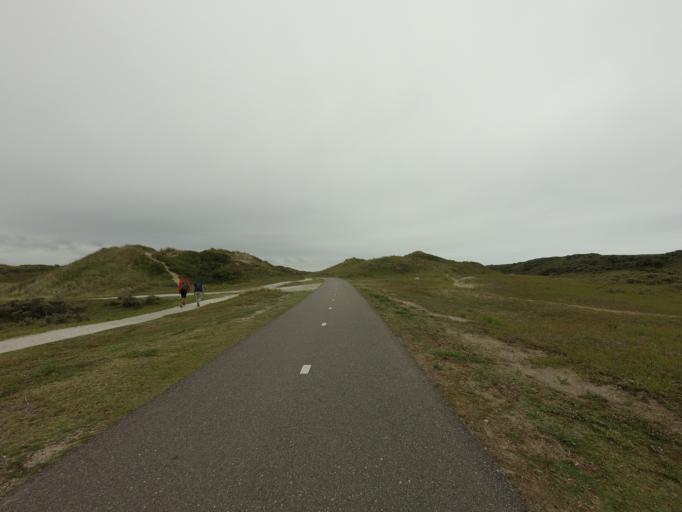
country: NL
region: South Holland
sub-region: Gemeente Katwijk
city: Katwijk aan Zee
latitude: 52.1831
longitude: 4.3751
